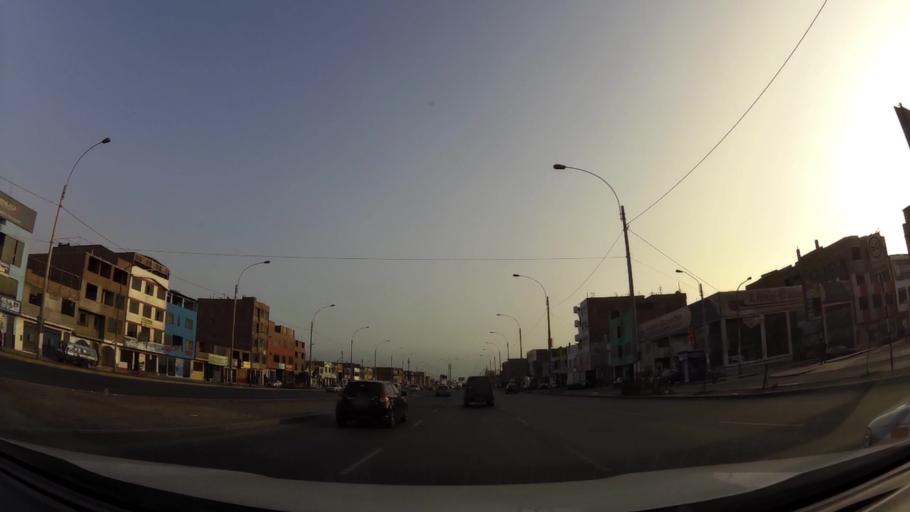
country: PE
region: Lima
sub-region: Lima
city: Independencia
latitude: -11.9928
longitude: -77.1091
